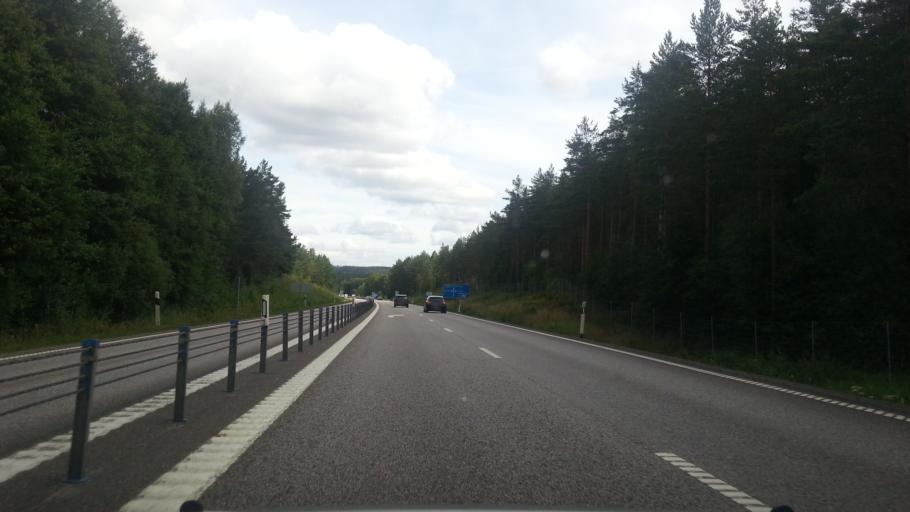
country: SE
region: Vaestra Goetaland
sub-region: Gullspangs Kommun
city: Anderstorp
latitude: 58.9241
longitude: 14.4099
